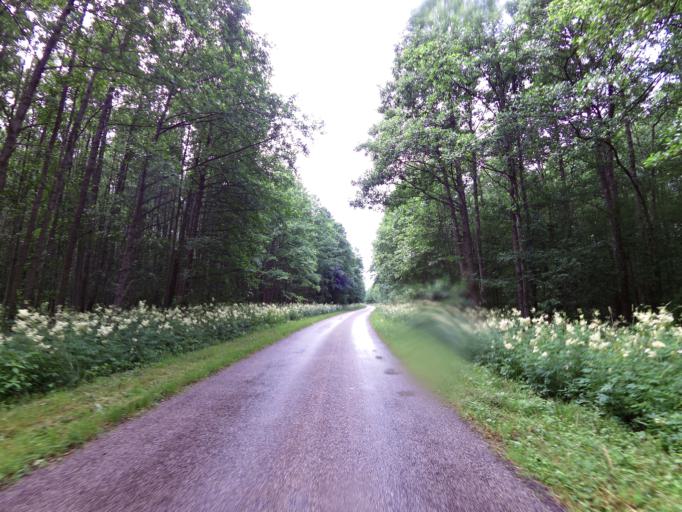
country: EE
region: Laeaene
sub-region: Vormsi vald
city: Hullo
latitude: 58.9910
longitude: 23.3209
